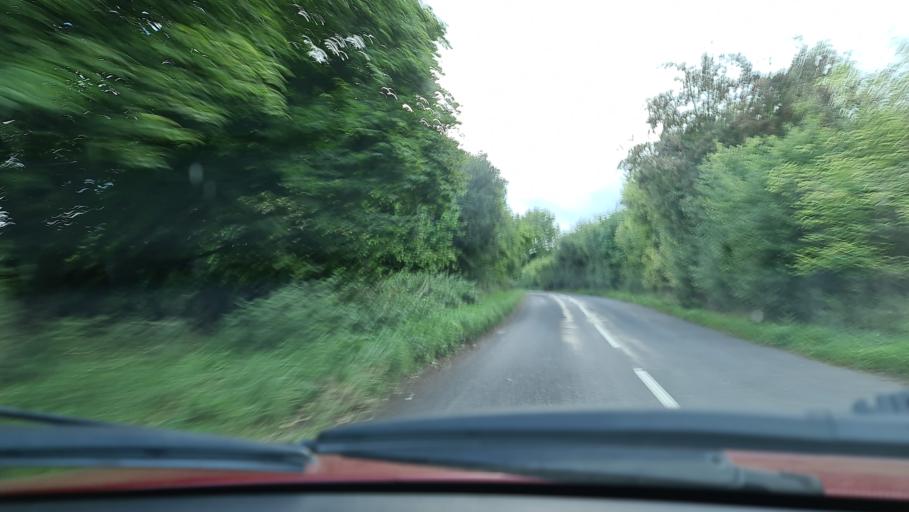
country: GB
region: England
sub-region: Buckinghamshire
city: Princes Risborough
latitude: 51.7338
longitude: -0.7961
